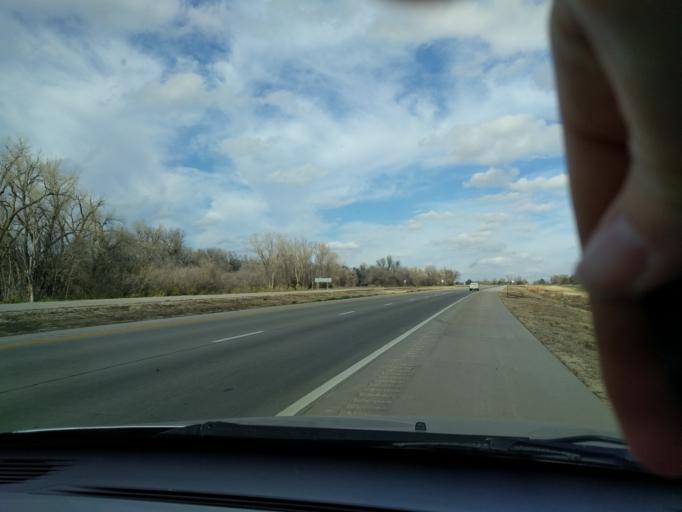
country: US
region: Kansas
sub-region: Reno County
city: Hutchinson
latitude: 38.0876
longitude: -97.8803
